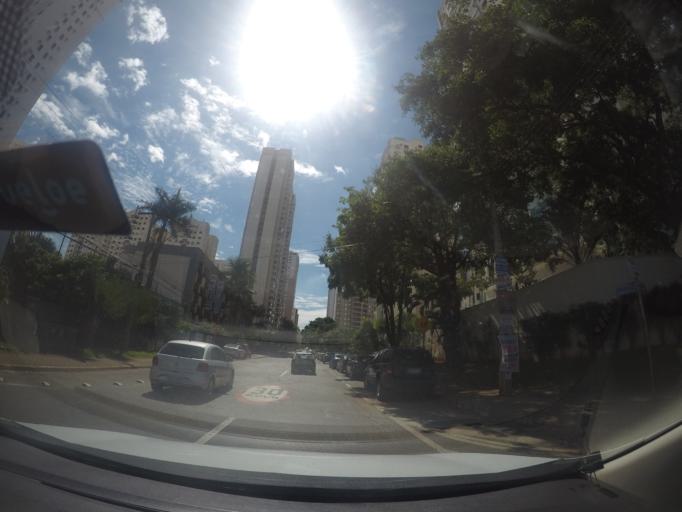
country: BR
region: Goias
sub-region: Goiania
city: Goiania
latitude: -16.7193
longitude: -49.2690
